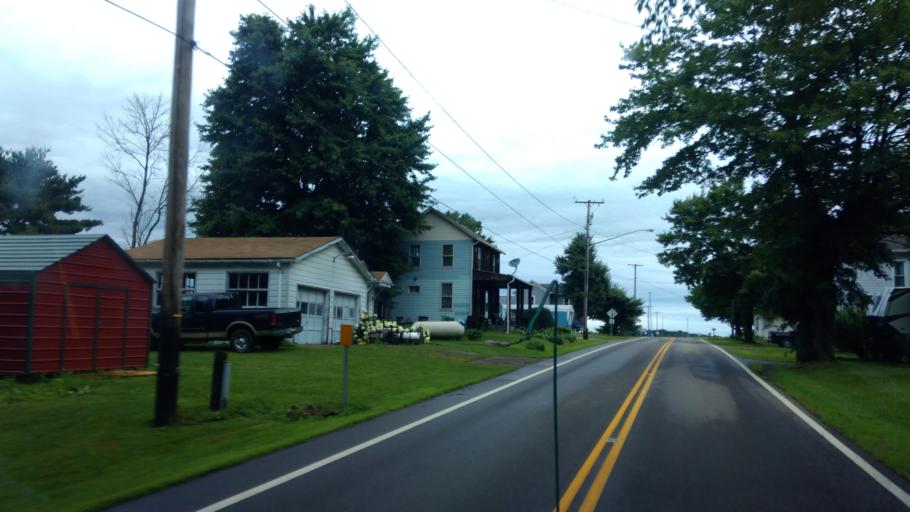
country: US
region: Ohio
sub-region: Stark County
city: Minerva
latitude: 40.6865
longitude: -81.0167
